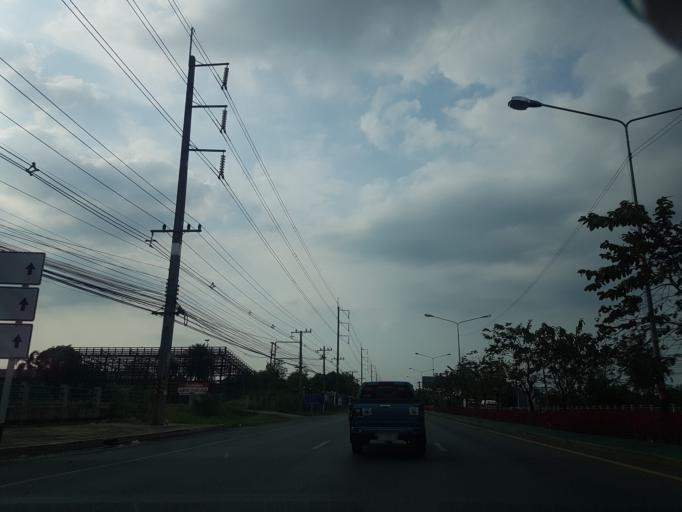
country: TH
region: Sara Buri
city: Phra Phutthabat
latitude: 14.7355
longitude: 100.7759
